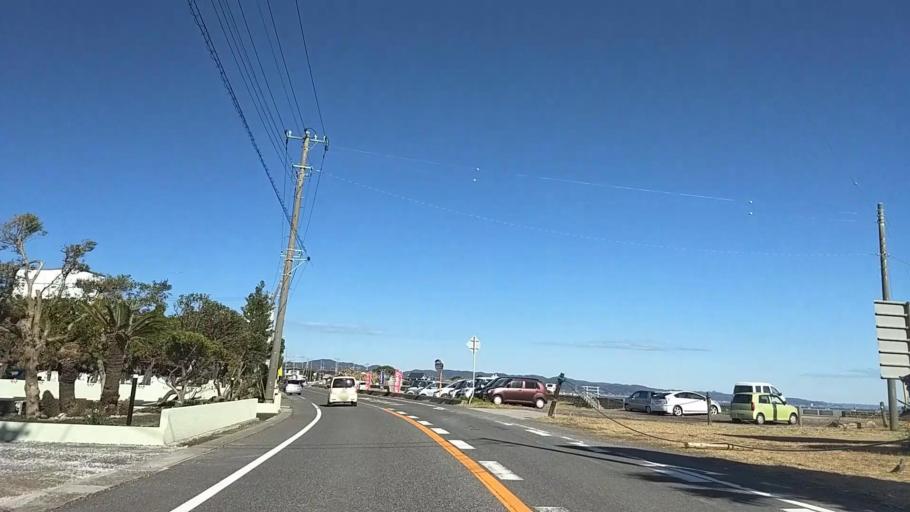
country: JP
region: Chiba
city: Tateyama
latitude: 34.9789
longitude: 139.9664
